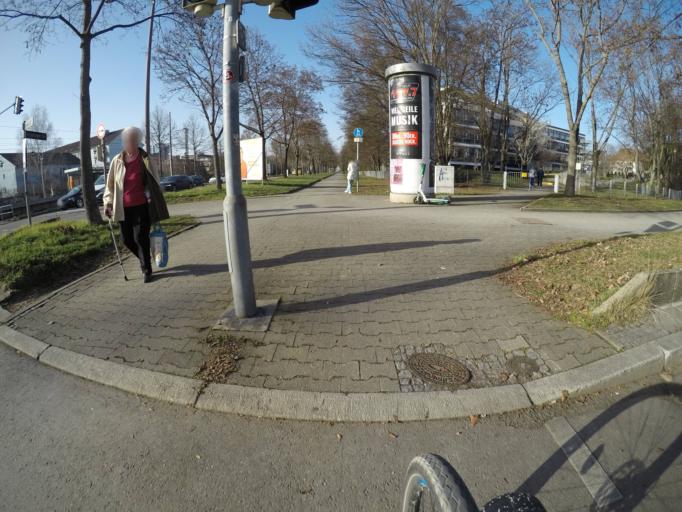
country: DE
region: Baden-Wuerttemberg
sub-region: Regierungsbezirk Stuttgart
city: Stuttgart-Ost
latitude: 48.7998
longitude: 9.2348
